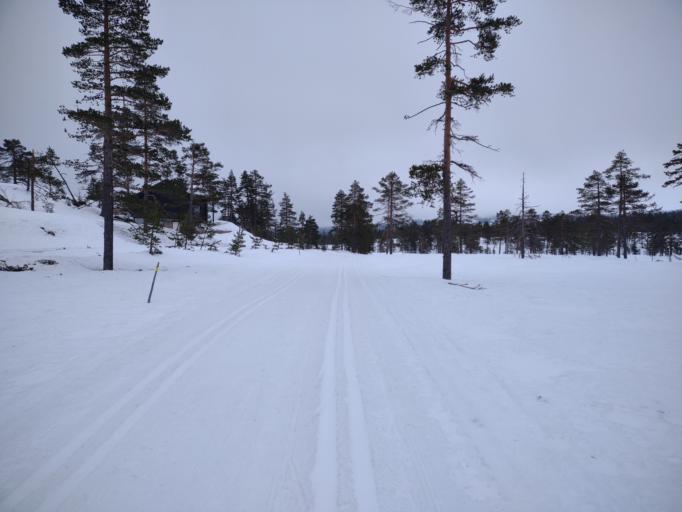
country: NO
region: Buskerud
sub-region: Flesberg
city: Lampeland
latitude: 59.7930
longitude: 9.4412
